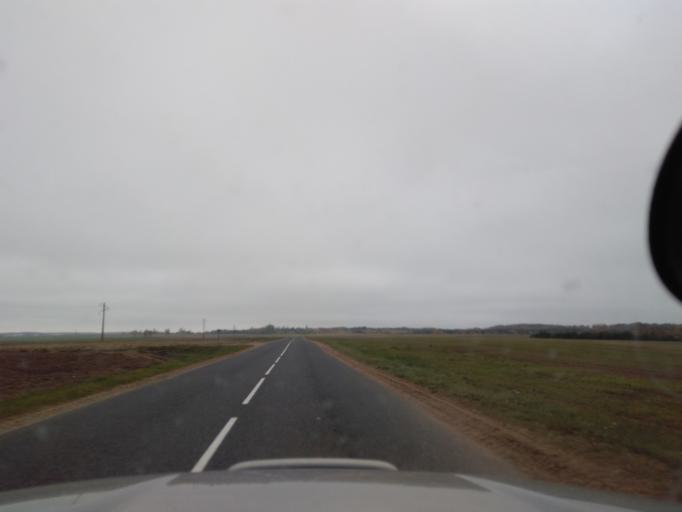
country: BY
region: Minsk
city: Kapyl'
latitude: 53.1521
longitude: 27.1873
